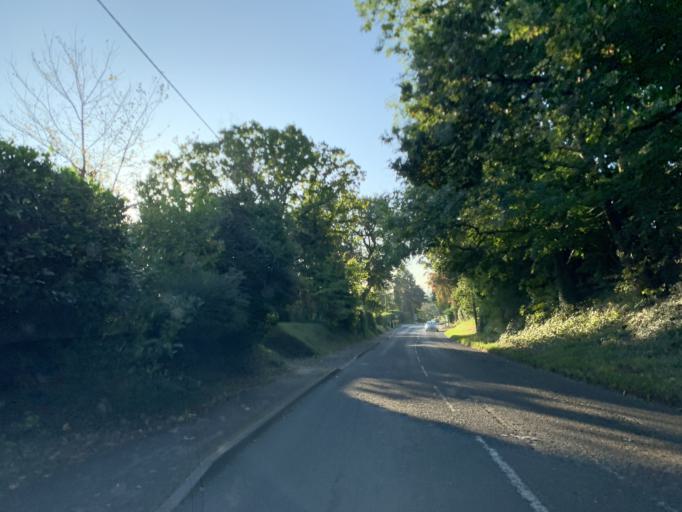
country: GB
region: England
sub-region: Wiltshire
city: Alderbury
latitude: 51.0434
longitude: -1.7328
